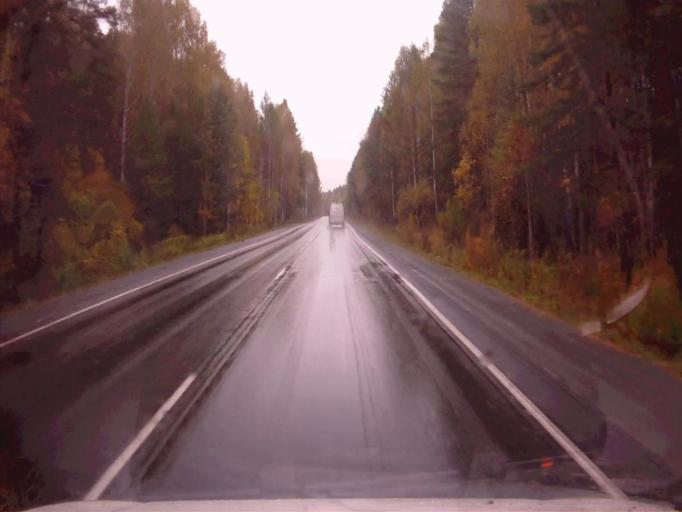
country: RU
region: Chelyabinsk
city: Tayginka
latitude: 55.5640
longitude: 60.6490
